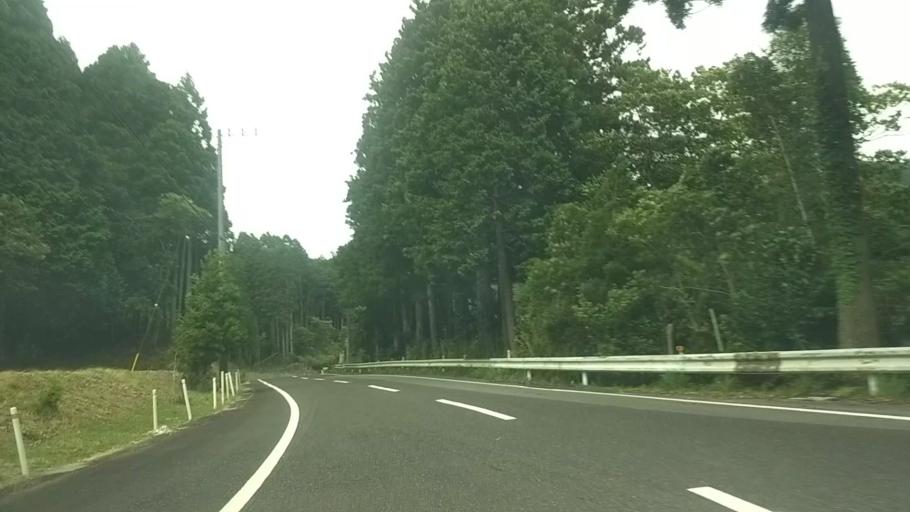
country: JP
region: Chiba
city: Kawaguchi
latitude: 35.1872
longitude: 140.1378
